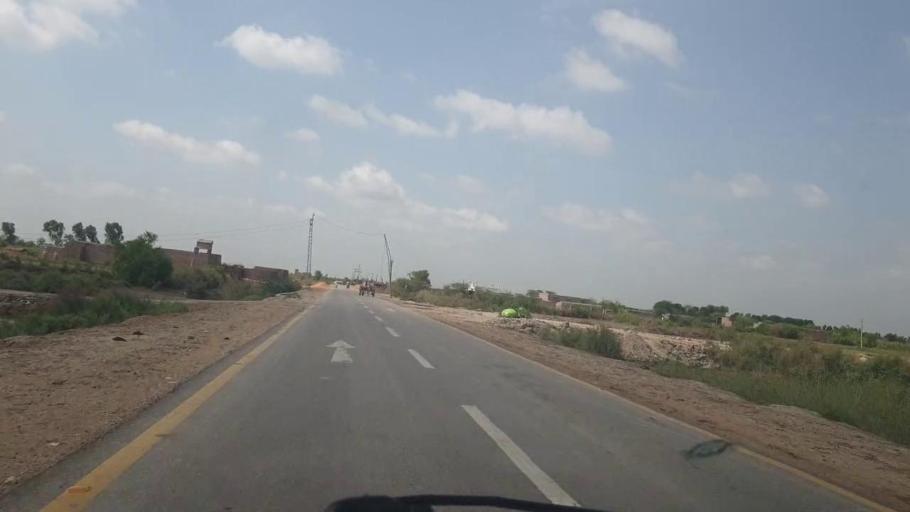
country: PK
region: Sindh
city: Berani
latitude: 25.6859
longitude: 68.9270
